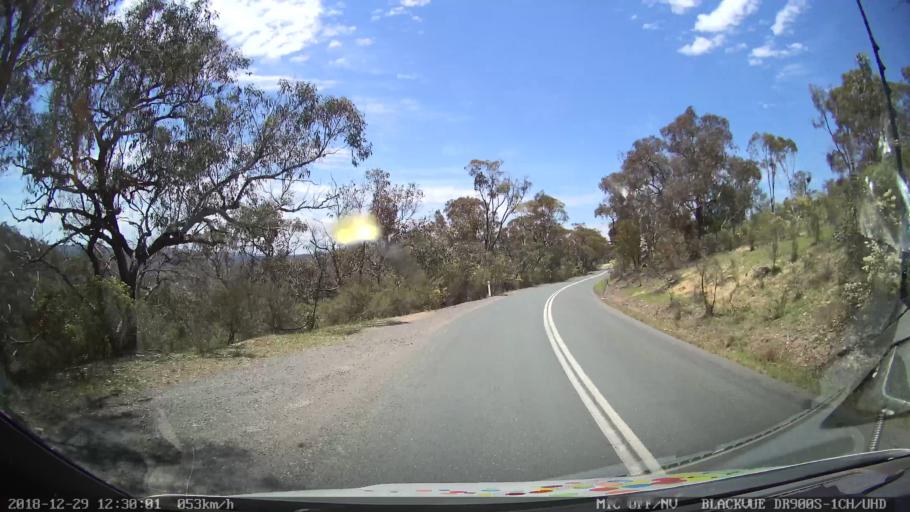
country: AU
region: Australian Capital Territory
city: Macarthur
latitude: -35.5026
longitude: 149.2326
